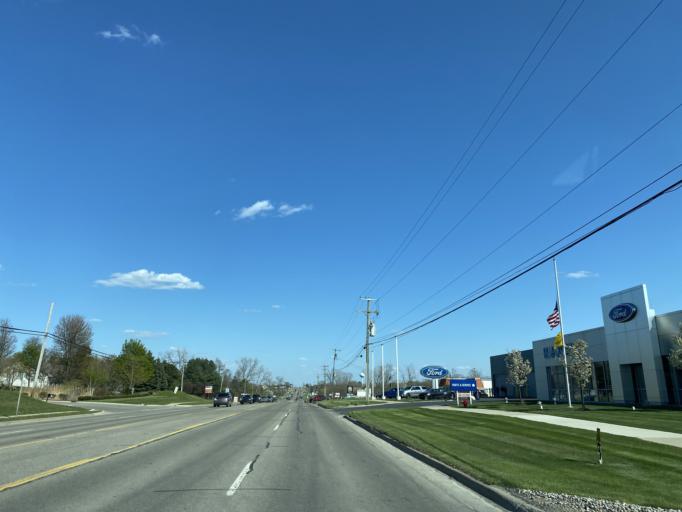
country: US
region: Michigan
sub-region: Livingston County
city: Howell
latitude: 42.5961
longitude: -83.8998
